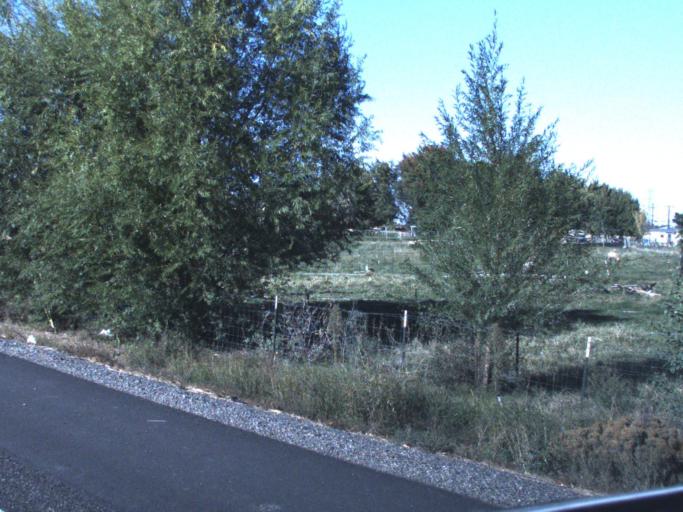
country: US
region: Washington
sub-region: Benton County
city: Finley
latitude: 46.1811
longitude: -119.0662
